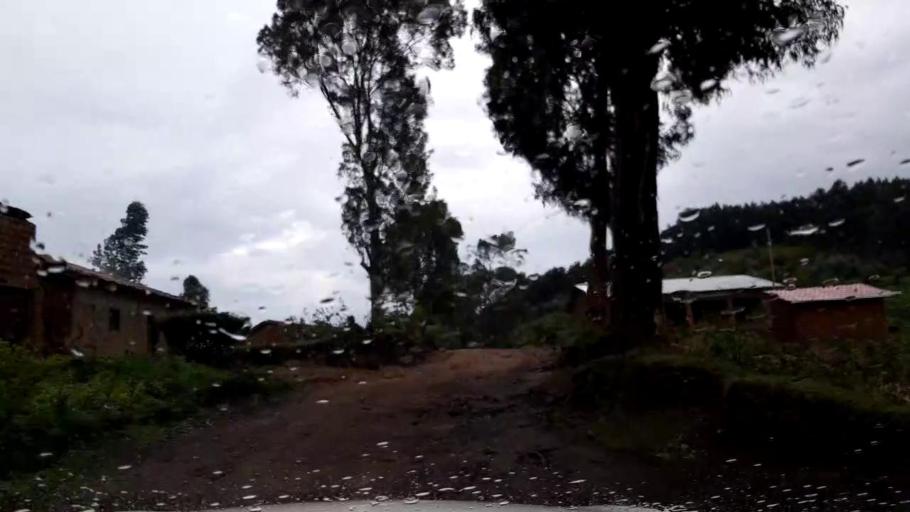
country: RW
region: Western Province
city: Kibuye
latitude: -2.0250
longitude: 29.4553
